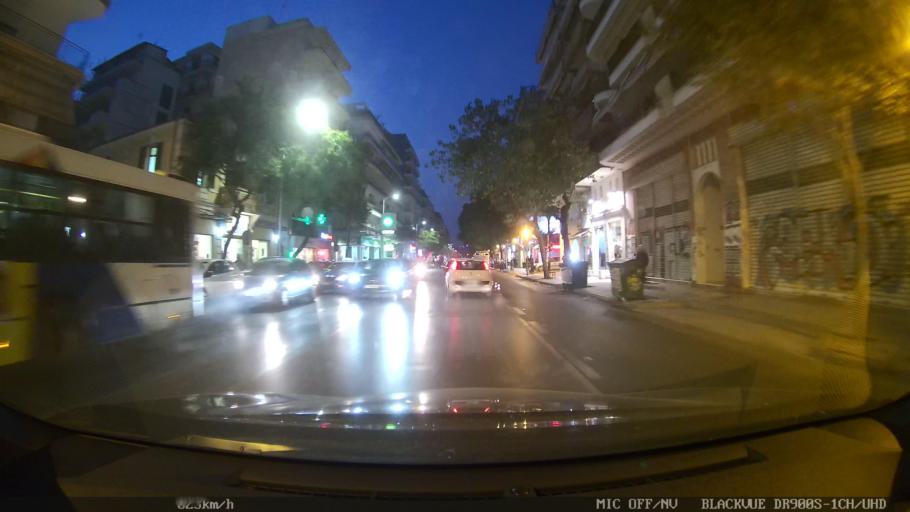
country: GR
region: Central Macedonia
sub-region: Nomos Thessalonikis
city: Triandria
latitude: 40.6187
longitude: 22.9584
